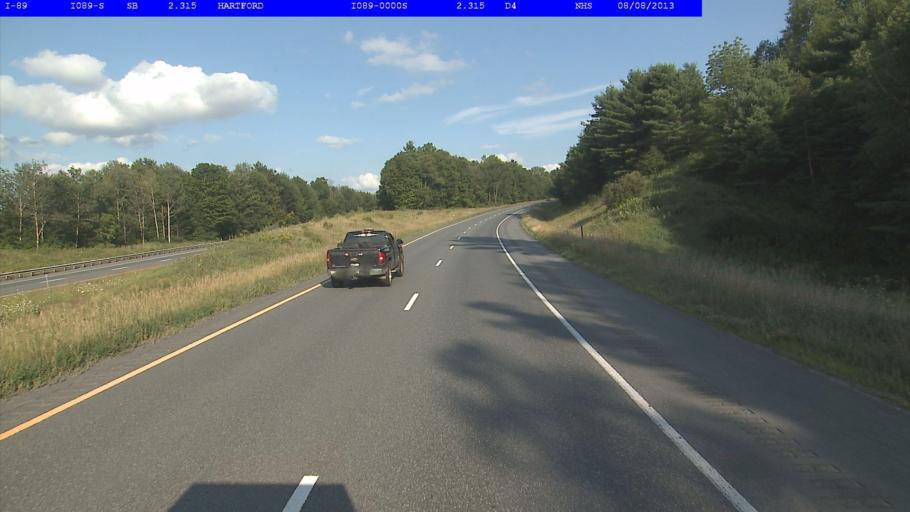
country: US
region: Vermont
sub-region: Windsor County
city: White River Junction
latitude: 43.6596
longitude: -72.3558
